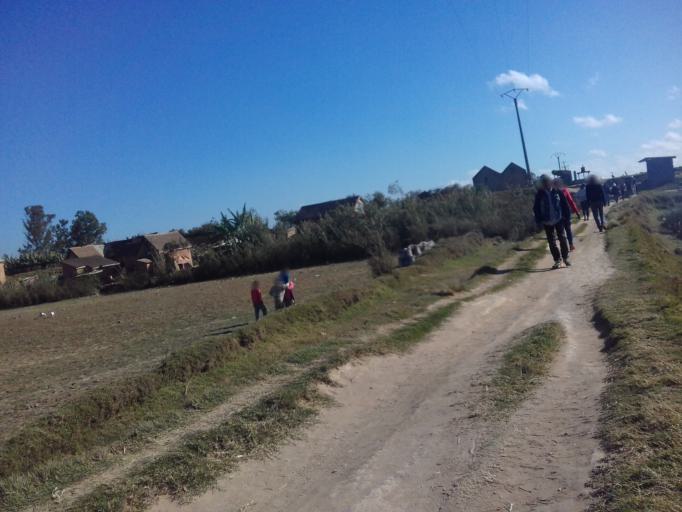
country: MG
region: Analamanga
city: Antananarivo
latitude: -18.8890
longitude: 47.4860
